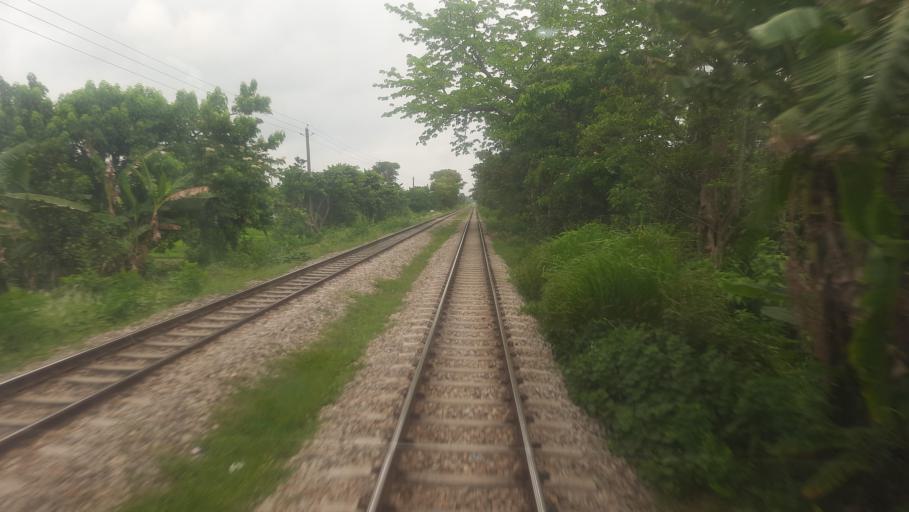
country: BD
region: Dhaka
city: Bhairab Bazar
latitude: 23.9786
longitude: 91.0799
